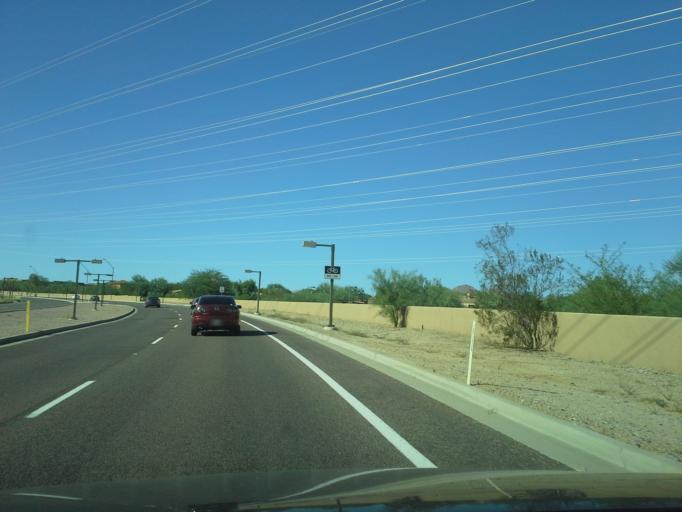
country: US
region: Arizona
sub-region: Maricopa County
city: Paradise Valley
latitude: 33.6659
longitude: -111.9043
